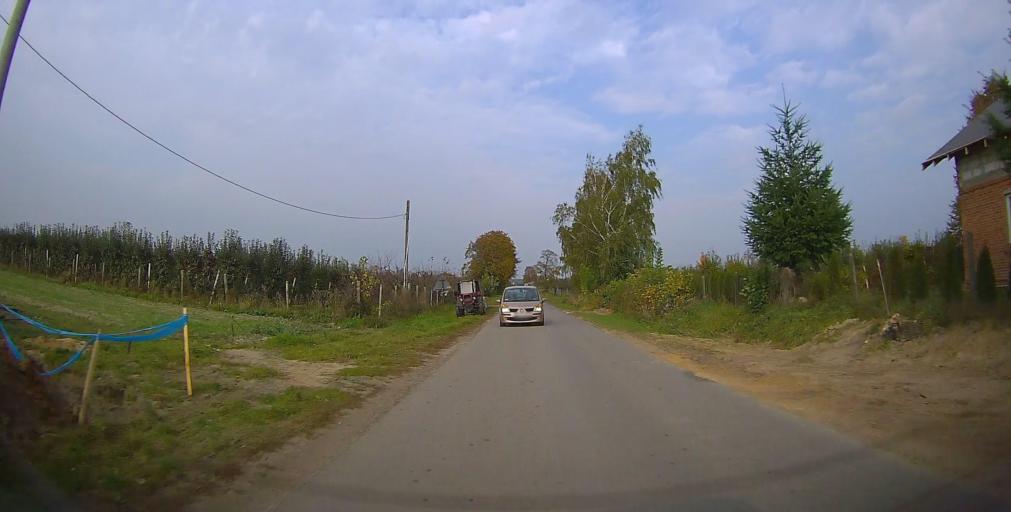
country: PL
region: Masovian Voivodeship
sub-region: Powiat grojecki
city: Mogielnica
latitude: 51.6475
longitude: 20.7328
